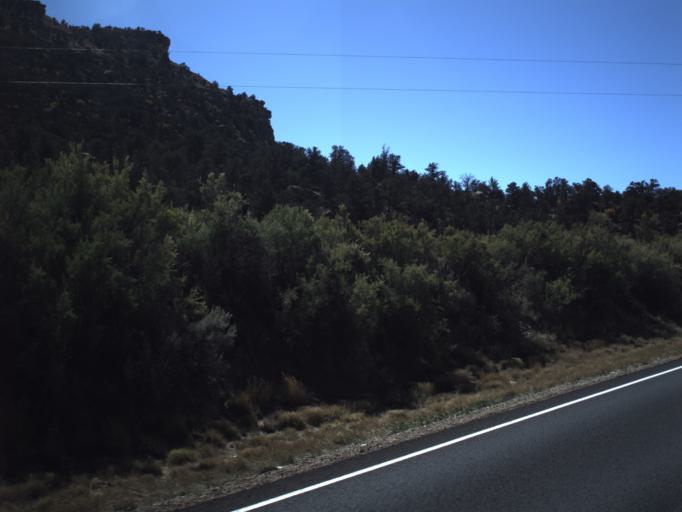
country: US
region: Utah
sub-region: Wayne County
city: Loa
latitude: 37.7616
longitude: -111.6933
